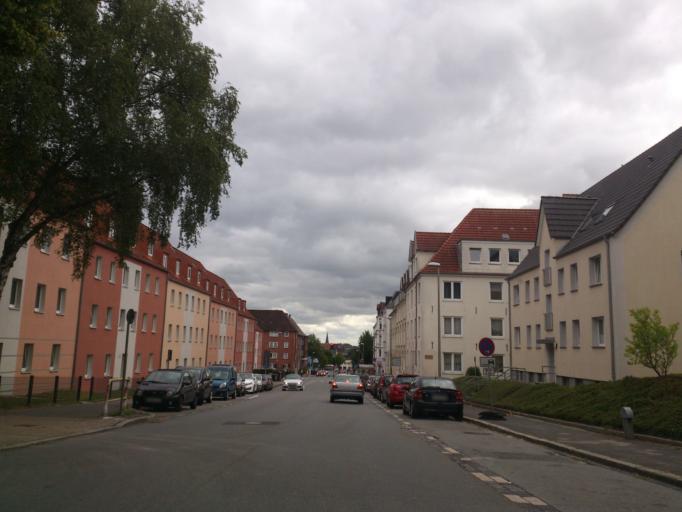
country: DE
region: Schleswig-Holstein
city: Flensburg
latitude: 54.7935
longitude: 9.4172
